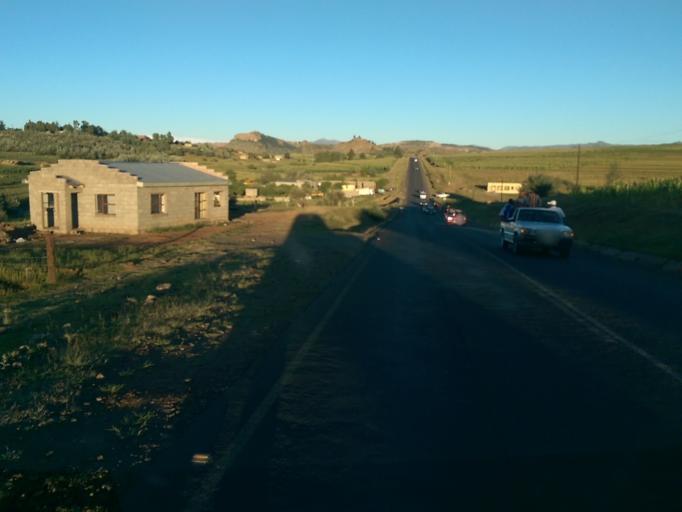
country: LS
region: Maseru
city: Maseru
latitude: -29.4084
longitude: 27.5950
